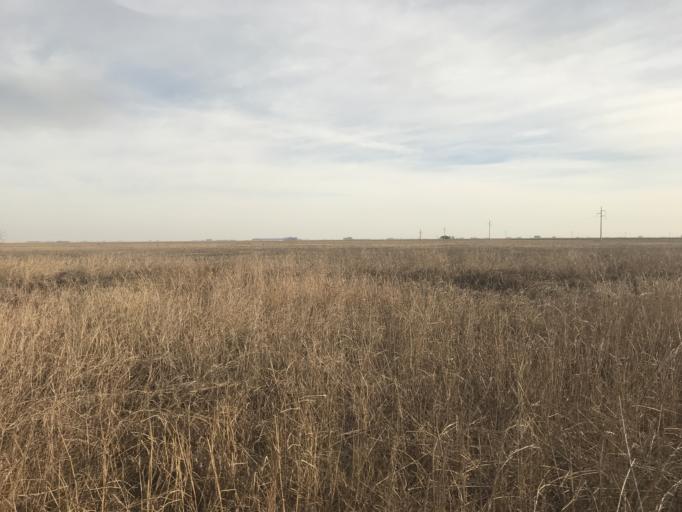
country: AR
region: Cordoba
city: Pilar
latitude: -31.7004
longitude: -63.8698
